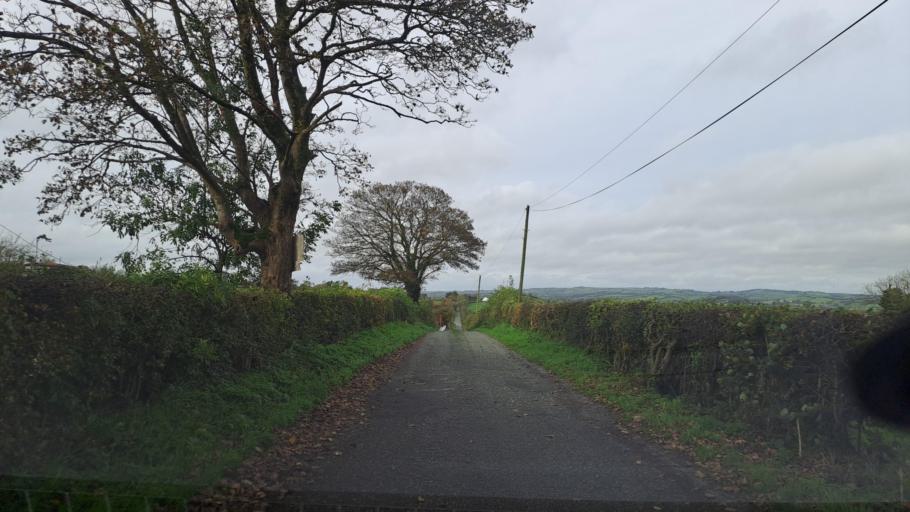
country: IE
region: Ulster
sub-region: County Monaghan
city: Carrickmacross
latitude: 54.0205
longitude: -6.8218
